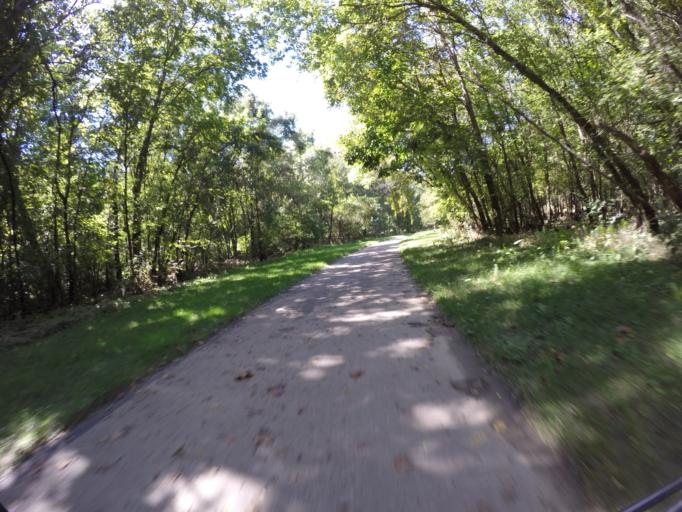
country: US
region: Kansas
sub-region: Johnson County
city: Lenexa
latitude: 38.9008
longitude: -94.7389
